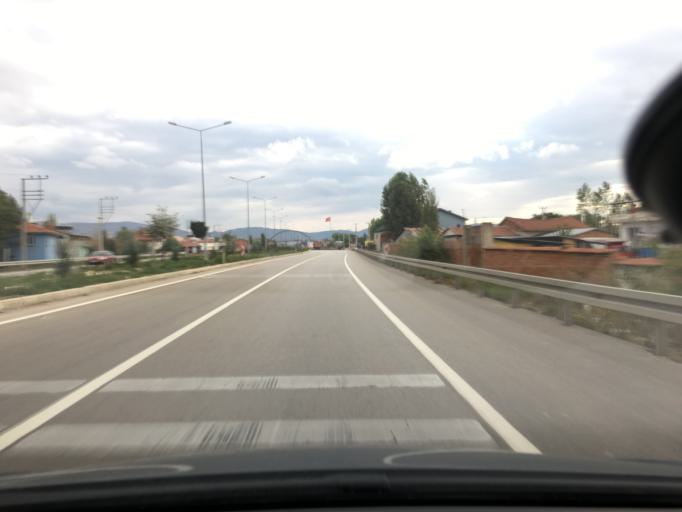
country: TR
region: Afyonkarahisar
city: Sincanli
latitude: 38.7792
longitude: 30.3736
